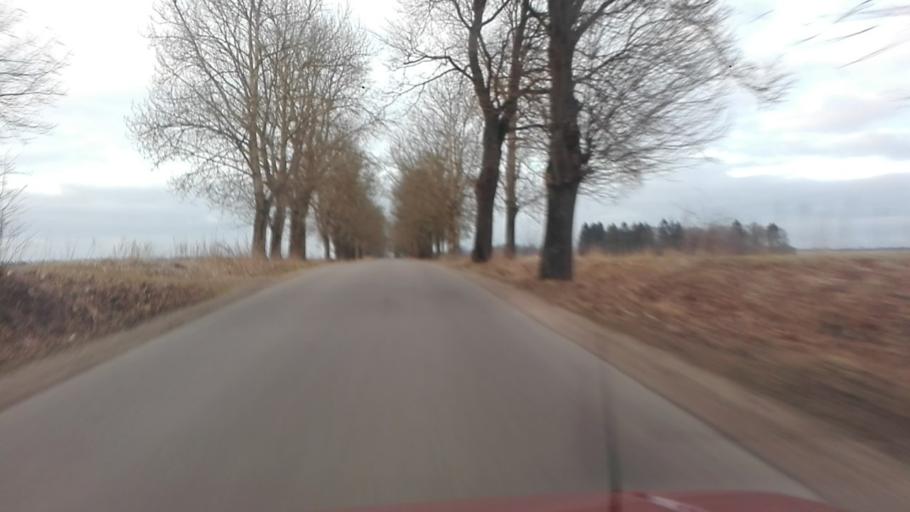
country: PL
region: West Pomeranian Voivodeship
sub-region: Powiat swidwinski
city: Rabino
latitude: 53.7839
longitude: 15.9005
